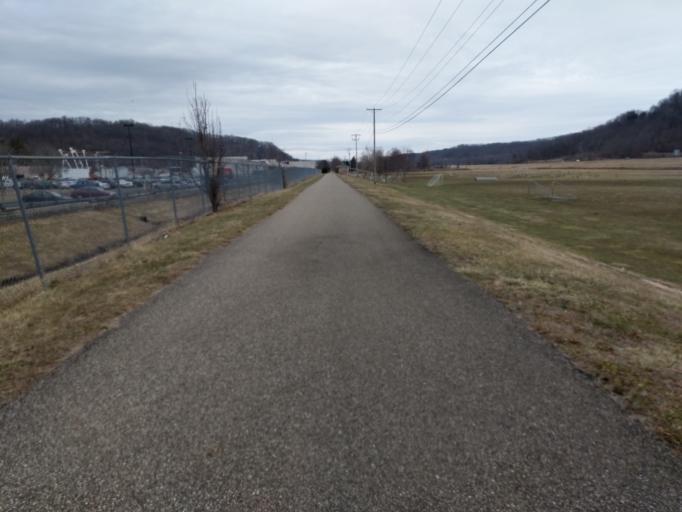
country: US
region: Ohio
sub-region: Athens County
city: Athens
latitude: 39.3347
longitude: -82.0658
